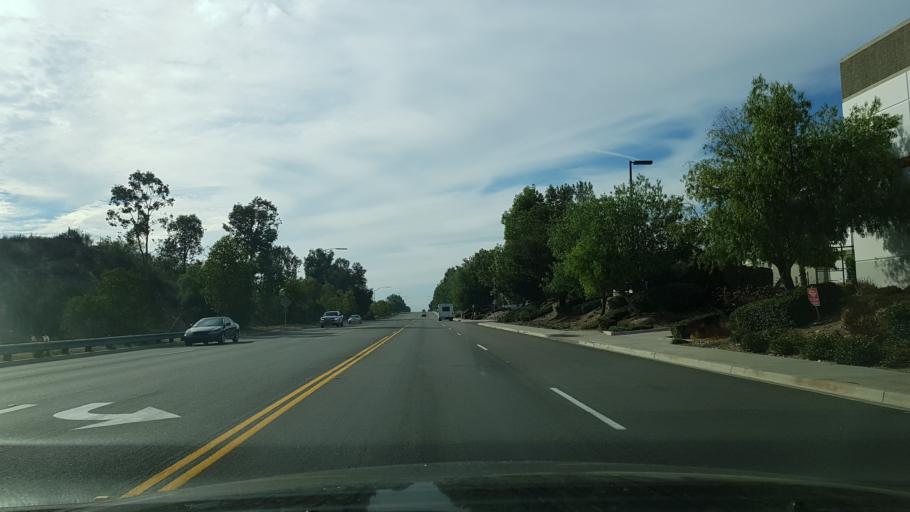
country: US
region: California
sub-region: San Diego County
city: Poway
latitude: 32.9348
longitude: -117.0369
